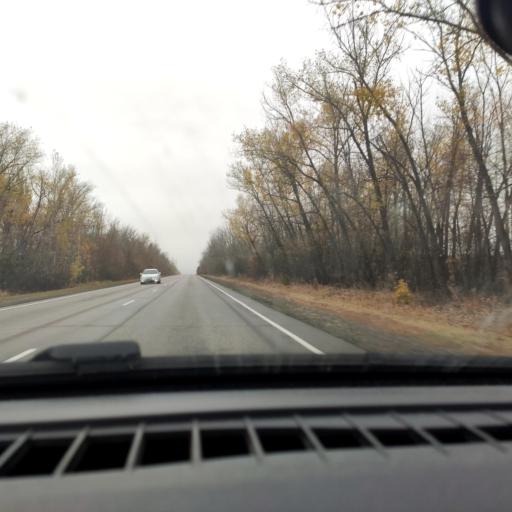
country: RU
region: Voronezj
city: Ostrogozhsk
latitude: 51.0117
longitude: 38.9924
